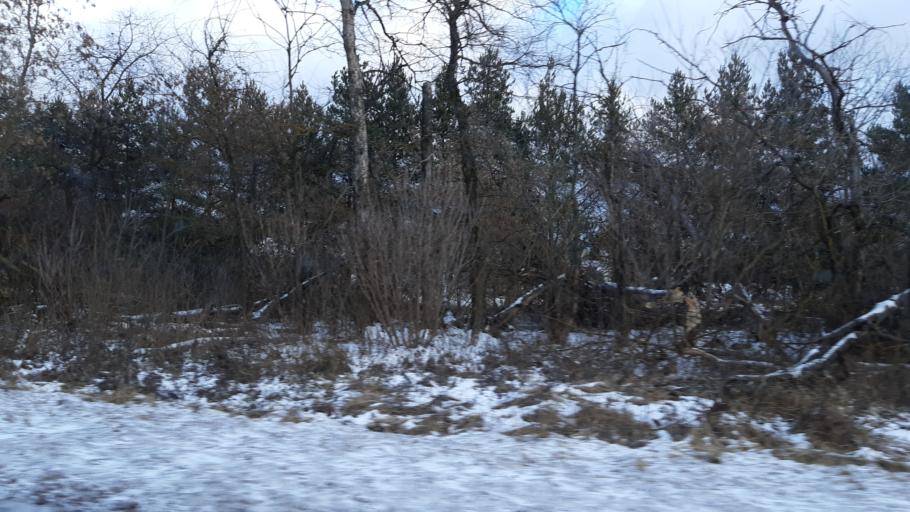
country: RU
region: Moskovskaya
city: Noginsk-9
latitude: 56.0138
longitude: 38.5582
